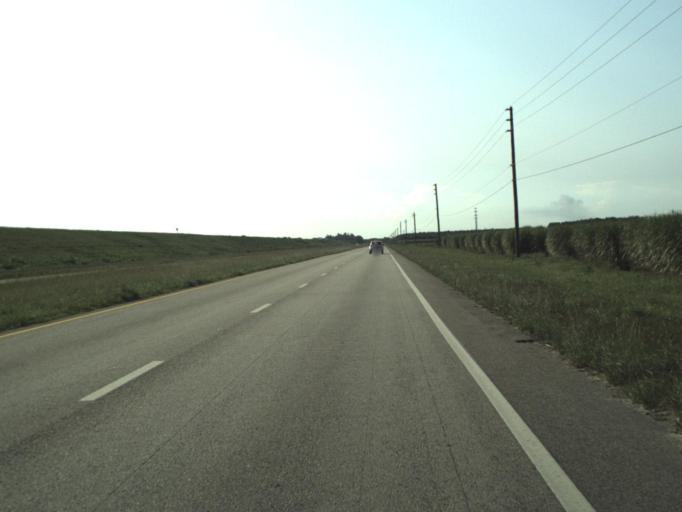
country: US
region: Florida
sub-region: Hendry County
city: Clewiston
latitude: 26.7110
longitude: -80.8353
